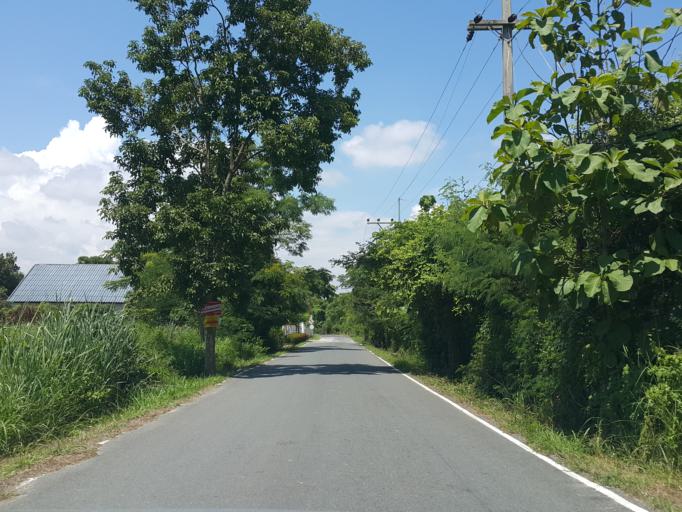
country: TH
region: Chiang Mai
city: San Sai
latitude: 18.8074
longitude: 99.0839
